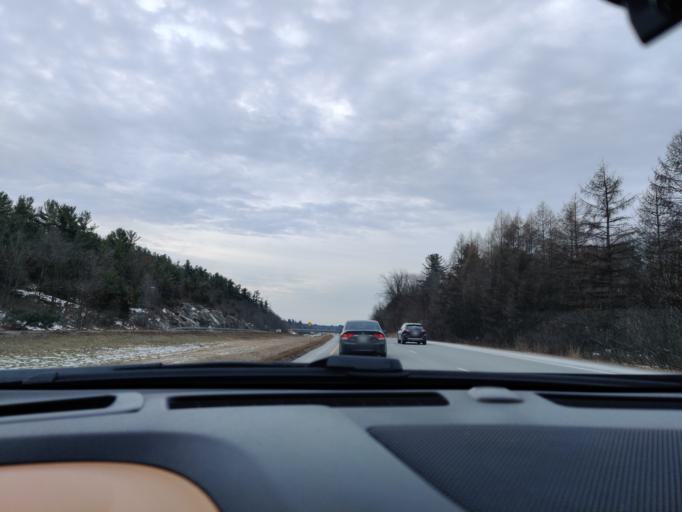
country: US
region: New York
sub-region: Jefferson County
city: Alexandria Bay
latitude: 44.4494
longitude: -75.8893
